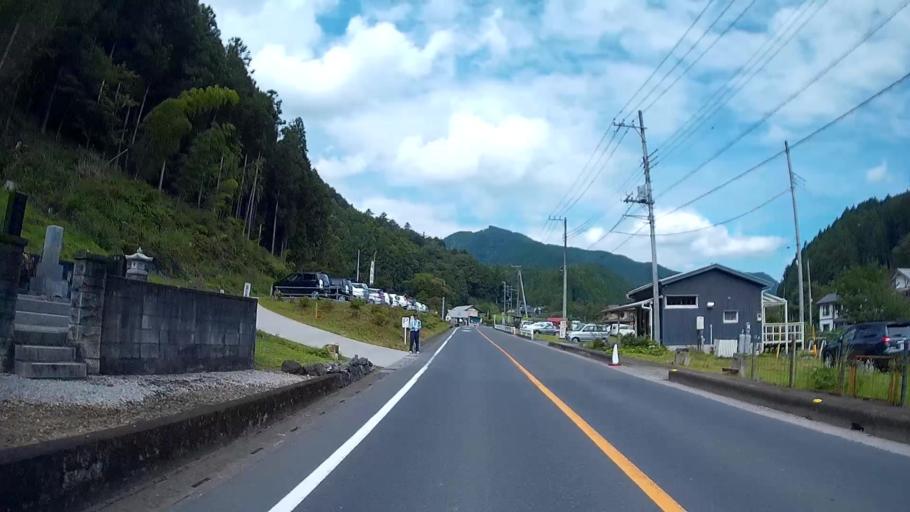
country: JP
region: Tokyo
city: Ome
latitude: 35.8537
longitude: 139.1960
